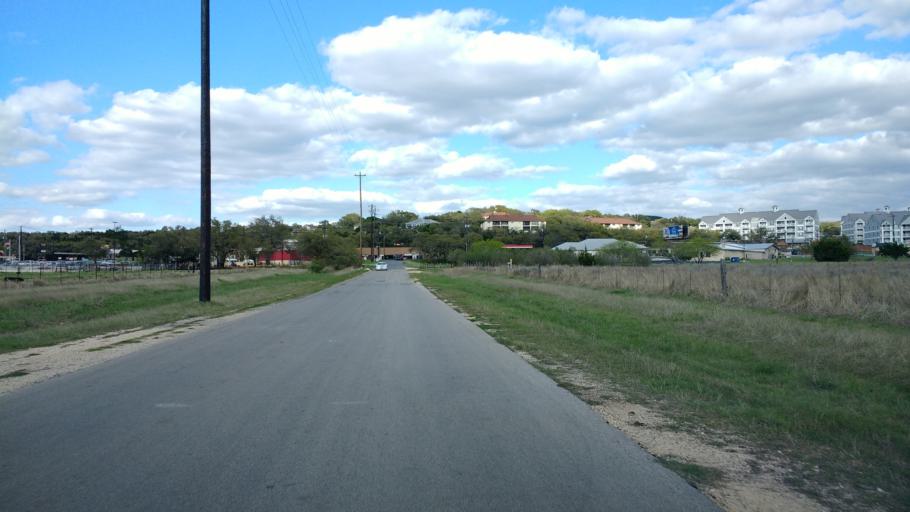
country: US
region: Texas
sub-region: Comal County
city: Canyon Lake
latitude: 29.9126
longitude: -98.2175
